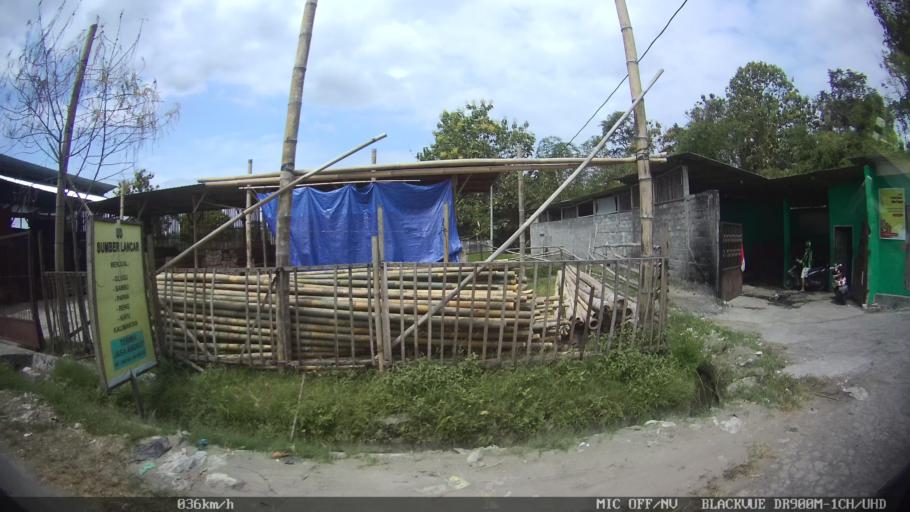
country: ID
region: Daerah Istimewa Yogyakarta
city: Depok
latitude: -7.8051
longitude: 110.4508
